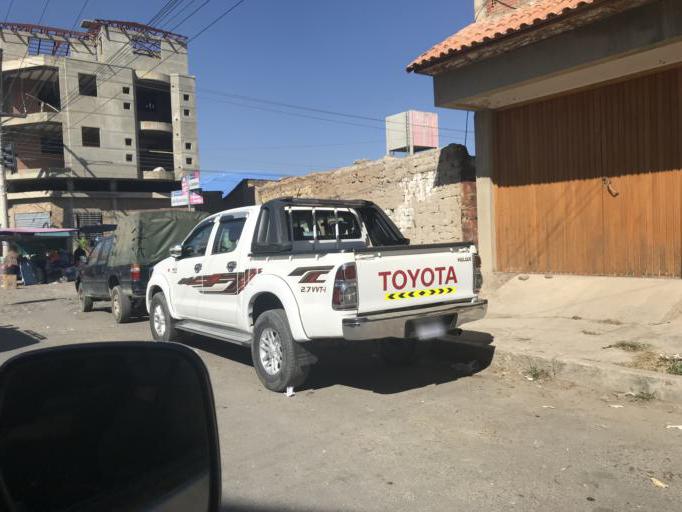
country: BO
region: Cochabamba
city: Punata
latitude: -17.5482
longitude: -65.8409
